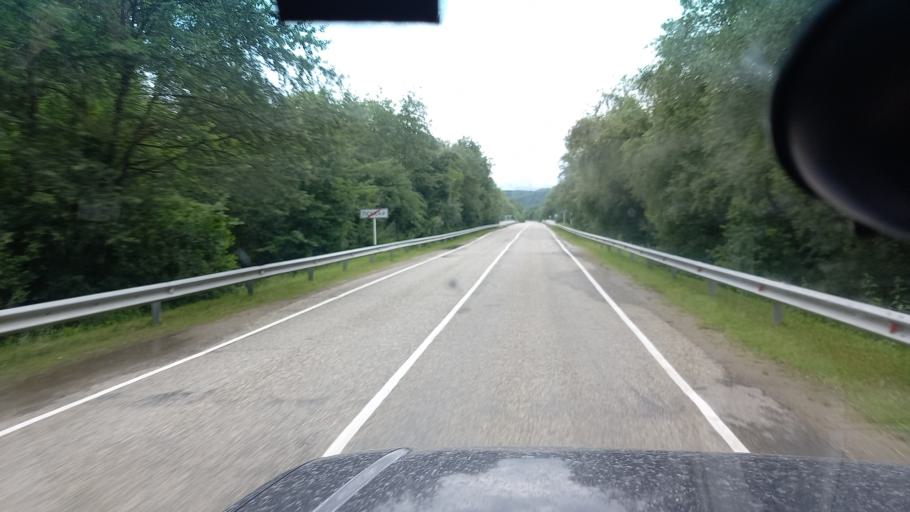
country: RU
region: Krasnodarskiy
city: Psebay
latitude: 44.0885
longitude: 40.7890
